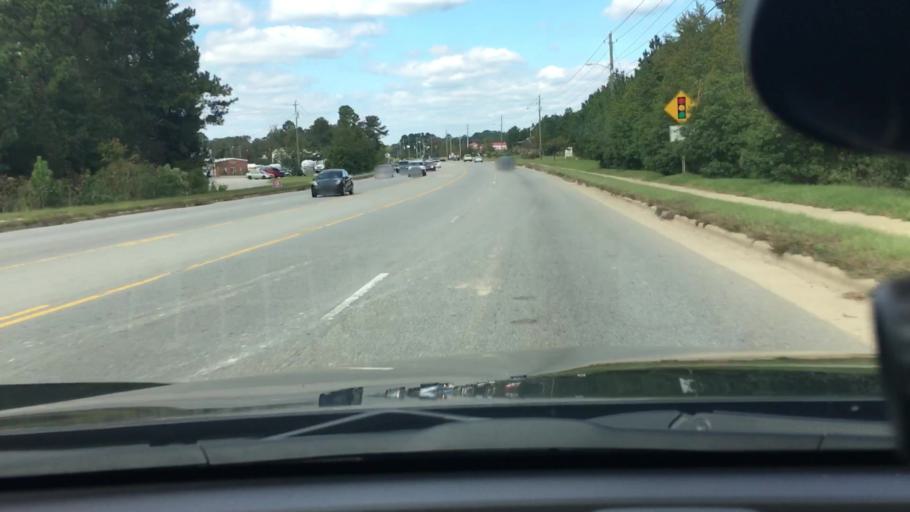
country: US
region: North Carolina
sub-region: Wake County
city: Apex
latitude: 35.7024
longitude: -78.8340
